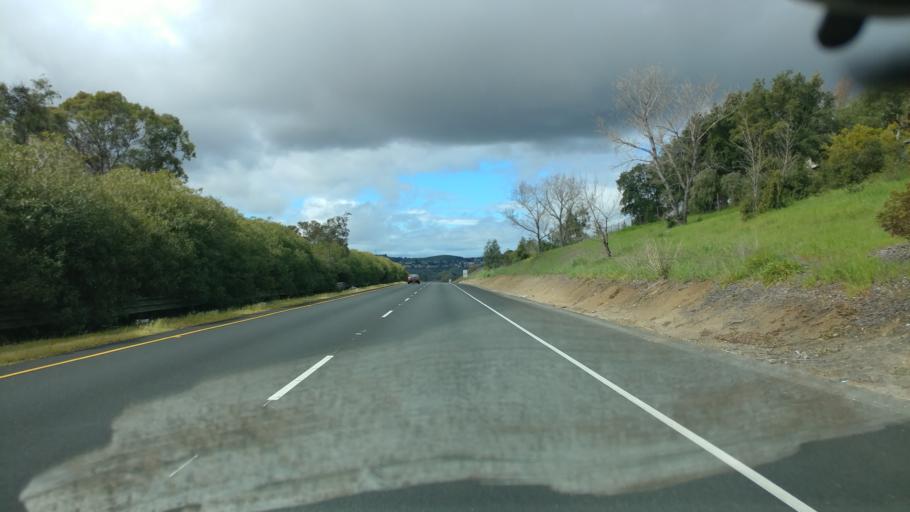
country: US
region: California
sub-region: Solano County
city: Benicia
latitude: 38.0659
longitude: -122.1697
